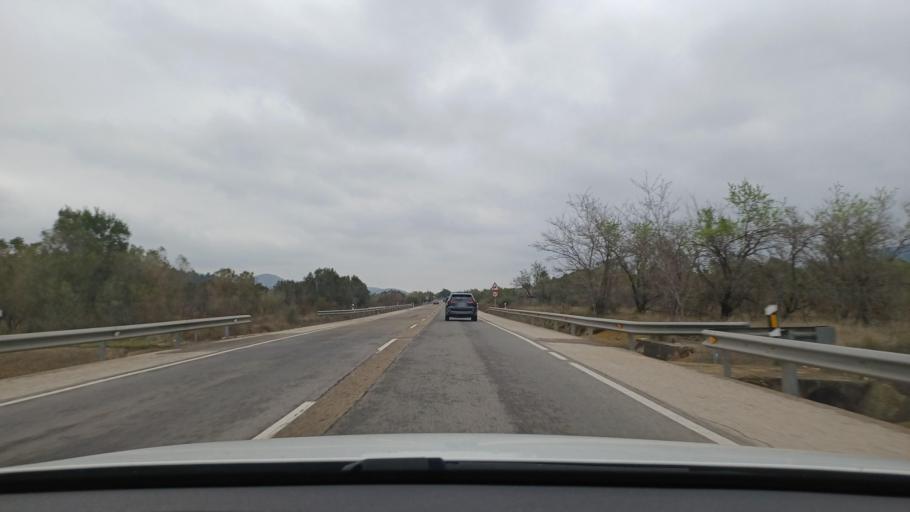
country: ES
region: Valencia
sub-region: Provincia de Castello
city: Santa Magdalena de Pulpis
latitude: 40.3391
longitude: 0.2639
